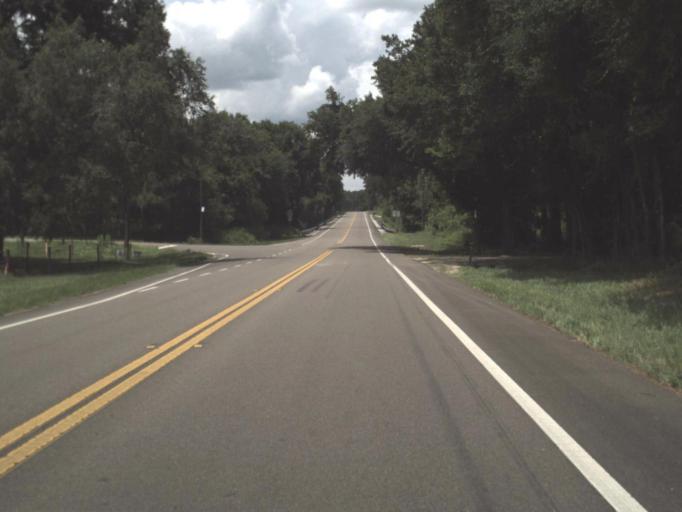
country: US
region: Florida
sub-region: Levy County
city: Williston
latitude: 29.4177
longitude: -82.4549
